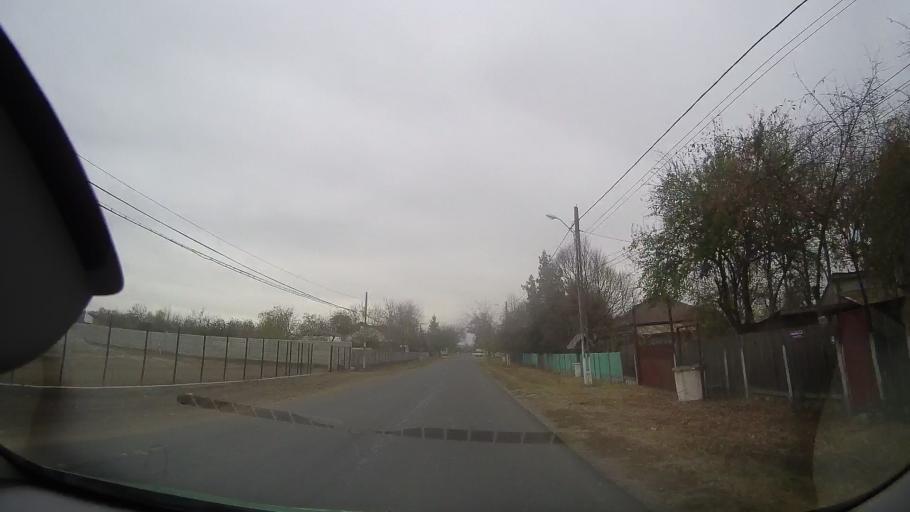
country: RO
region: Braila
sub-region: Comuna Ulmu
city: Ulmu
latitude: 44.9534
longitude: 27.3134
